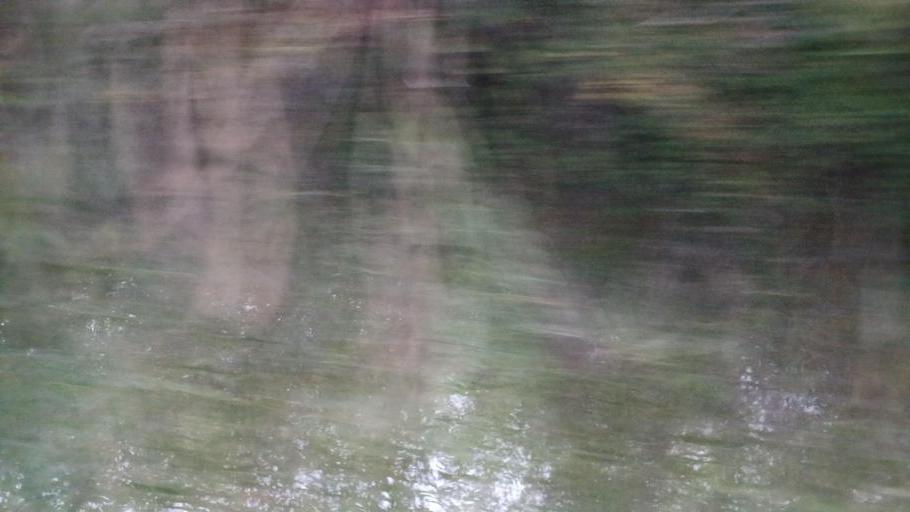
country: CY
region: Pafos
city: Tala
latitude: 34.9357
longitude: 32.5138
